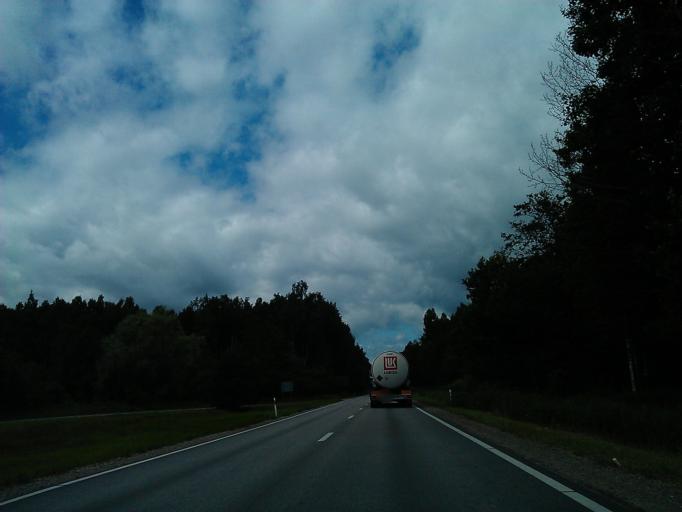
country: LV
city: Tireli
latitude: 56.9283
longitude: 23.5773
